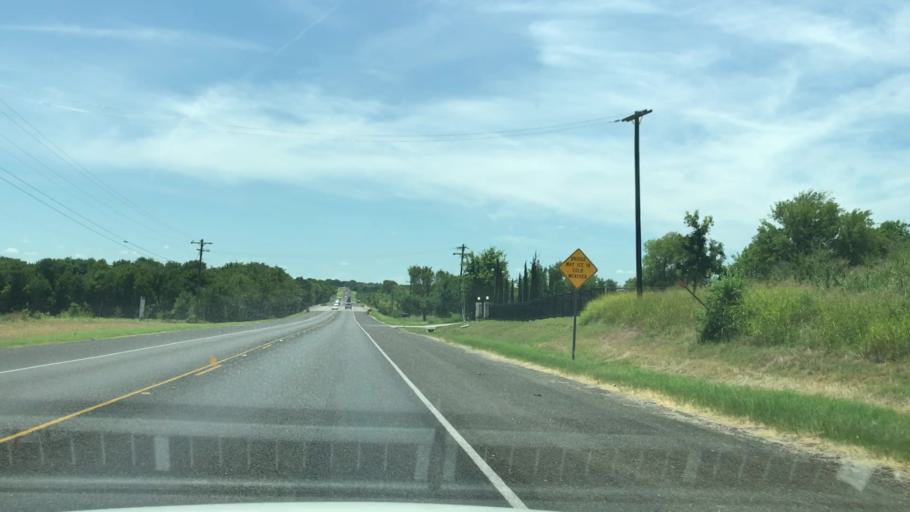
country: US
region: Texas
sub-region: Collin County
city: Lavon
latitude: 32.9876
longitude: -96.4668
